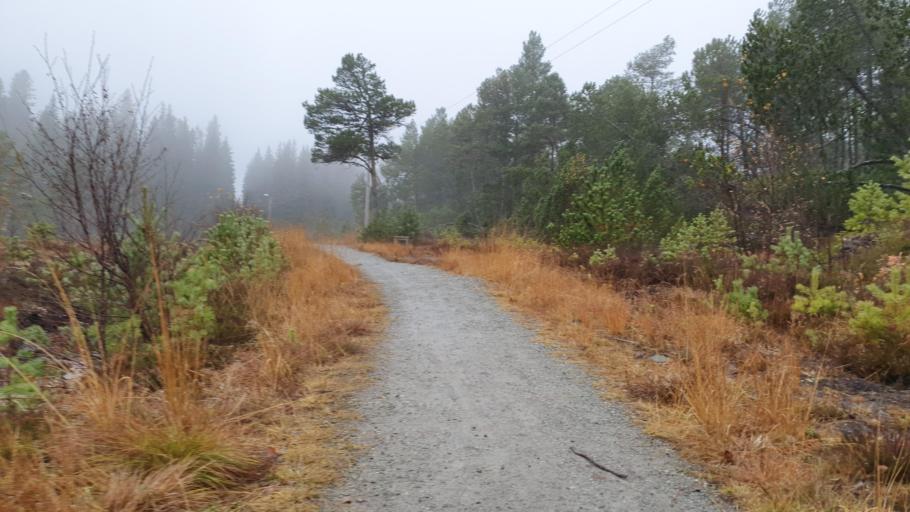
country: NO
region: Sor-Trondelag
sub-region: Trondheim
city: Trondheim
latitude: 63.4134
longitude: 10.3166
